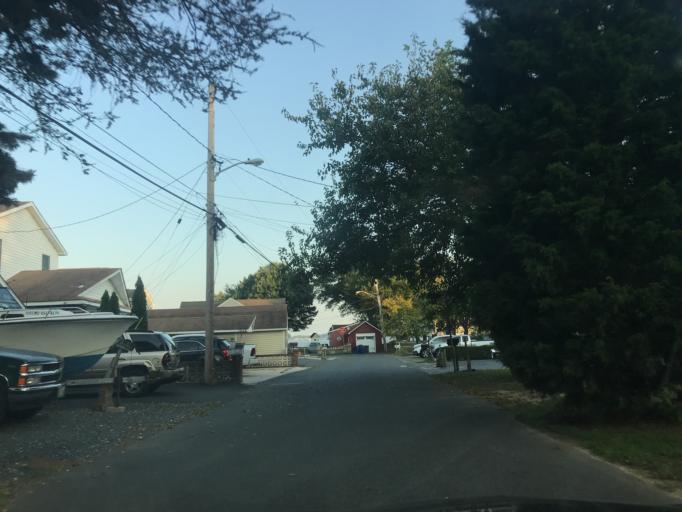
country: US
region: Maryland
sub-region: Baltimore County
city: Bowleys Quarters
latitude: 39.3093
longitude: -76.4113
